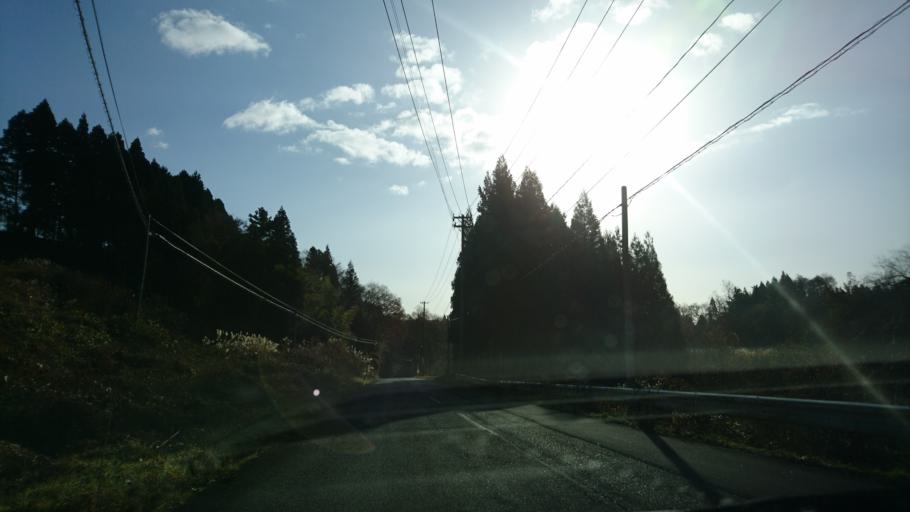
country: JP
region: Iwate
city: Ichinoseki
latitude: 38.8695
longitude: 141.3249
